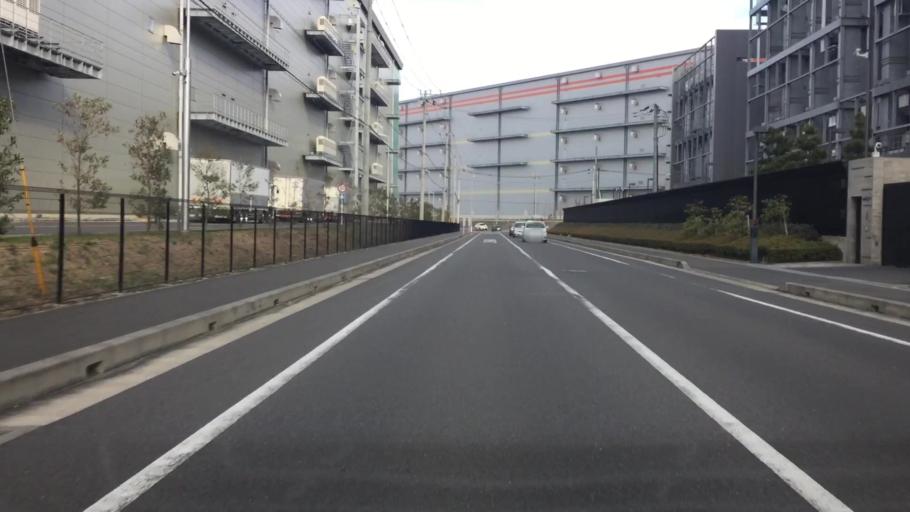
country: JP
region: Chiba
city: Shiroi
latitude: 35.8069
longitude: 140.1242
